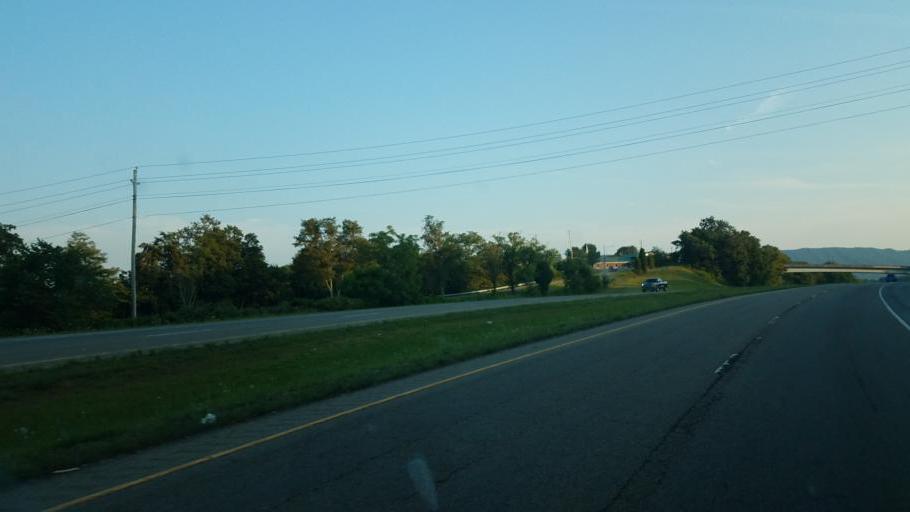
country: US
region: Tennessee
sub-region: Sullivan County
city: Kingsport
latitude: 36.5772
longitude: -82.5793
